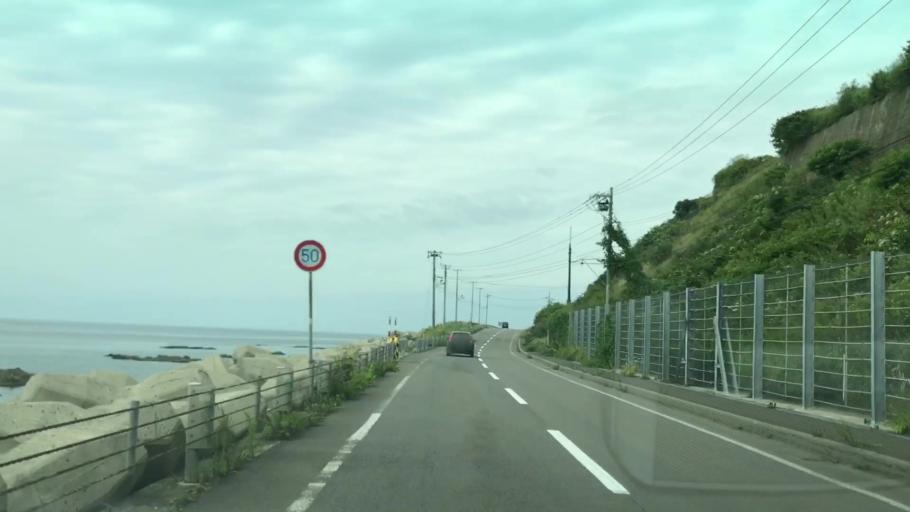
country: JP
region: Hokkaido
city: Iwanai
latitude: 43.1630
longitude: 140.3888
